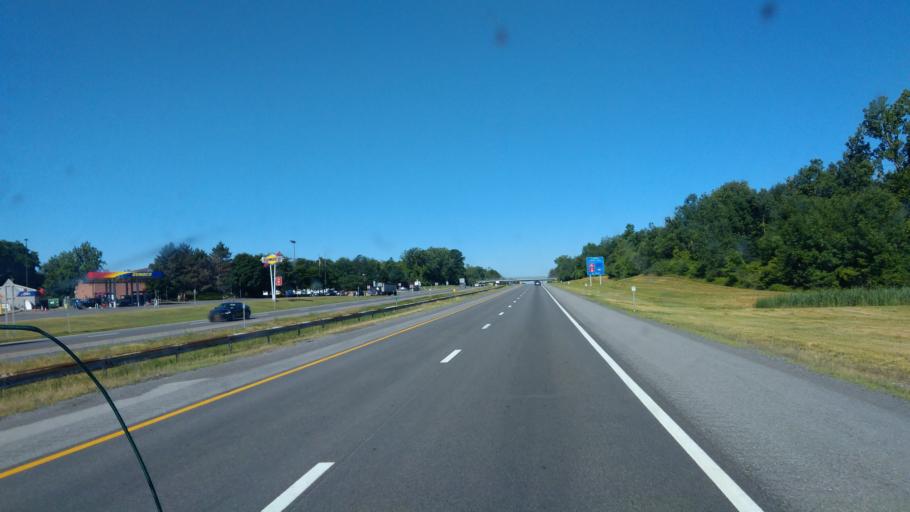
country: US
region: New York
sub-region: Genesee County
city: Oakfield
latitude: 43.0128
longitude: -78.3268
